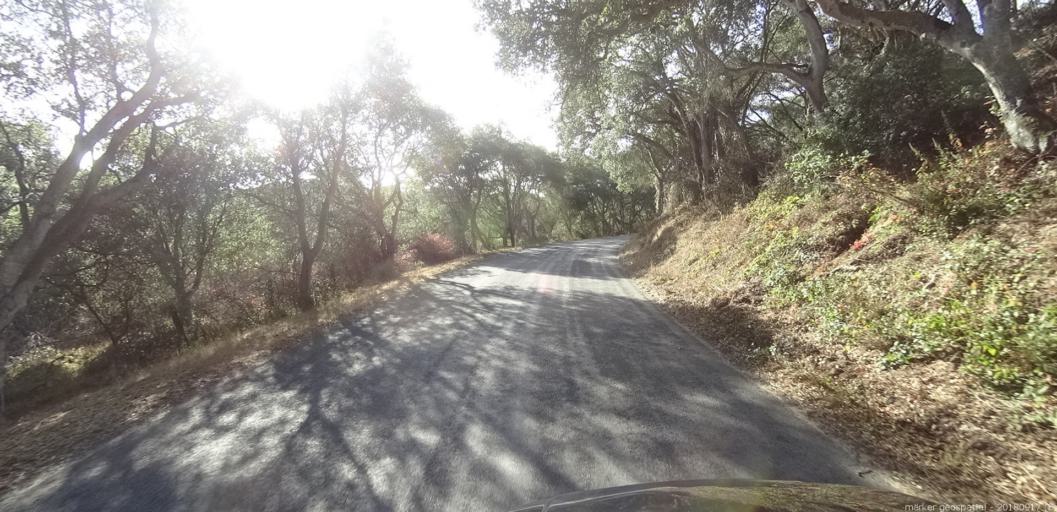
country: US
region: California
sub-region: Monterey County
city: Elkhorn
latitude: 36.8122
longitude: -121.7153
